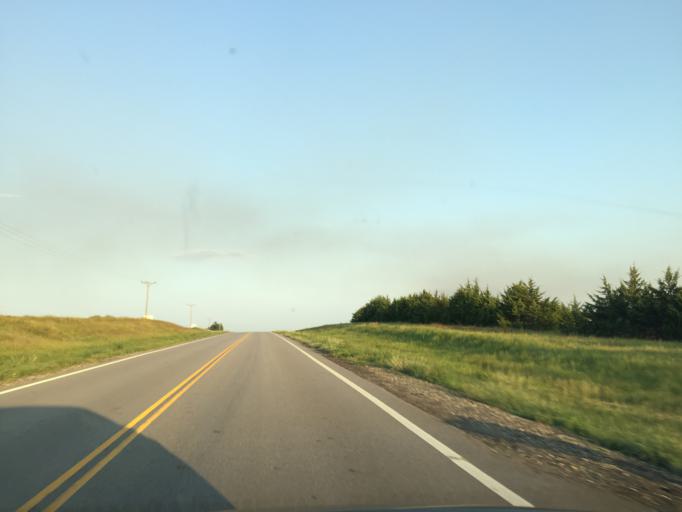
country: US
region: Kansas
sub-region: Ellsworth County
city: Ellsworth
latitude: 38.6984
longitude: -98.2130
